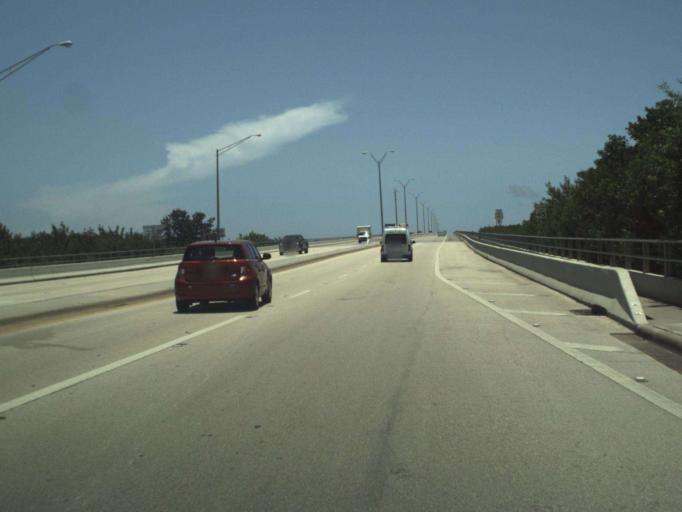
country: US
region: Florida
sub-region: Indian River County
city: Vero Beach
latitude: 27.6517
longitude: -80.3829
